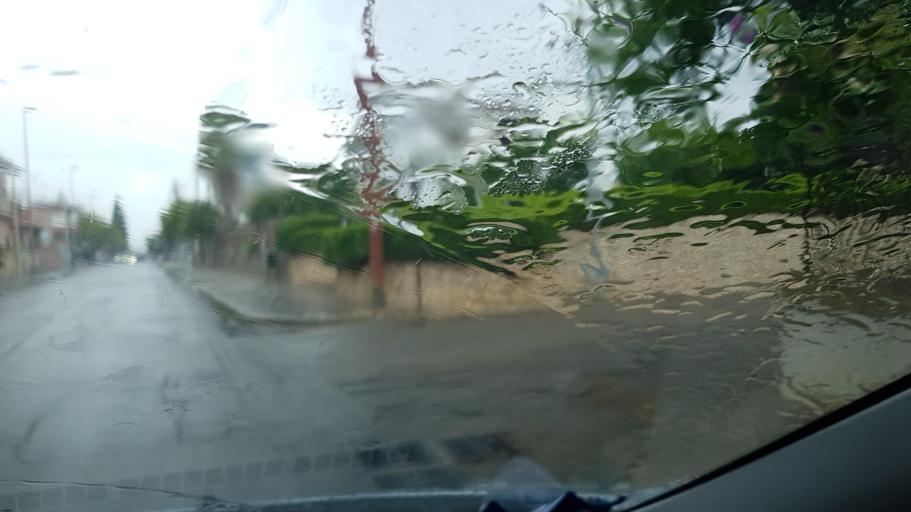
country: IT
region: Apulia
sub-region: Provincia di Lecce
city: Taurisano
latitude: 39.9564
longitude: 18.2204
